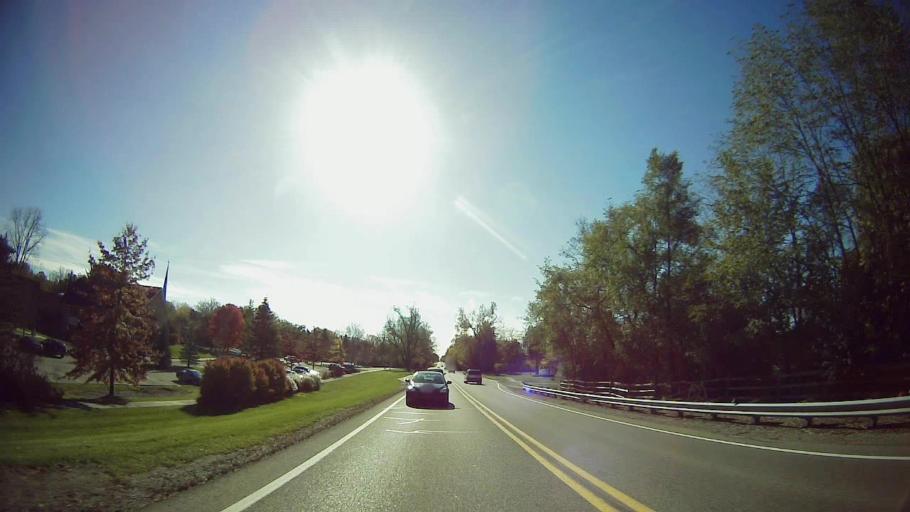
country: US
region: Michigan
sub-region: Oakland County
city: Farmington Hills
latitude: 42.5240
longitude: -83.3795
